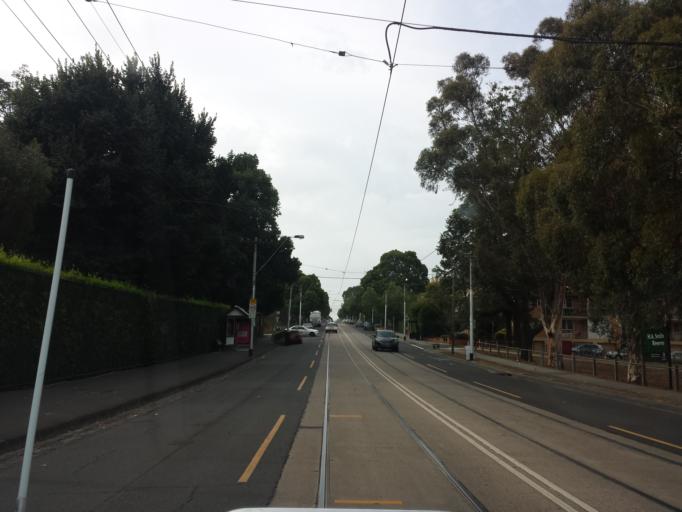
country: AU
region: Victoria
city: Glenferrie
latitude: -37.8361
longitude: 145.0329
